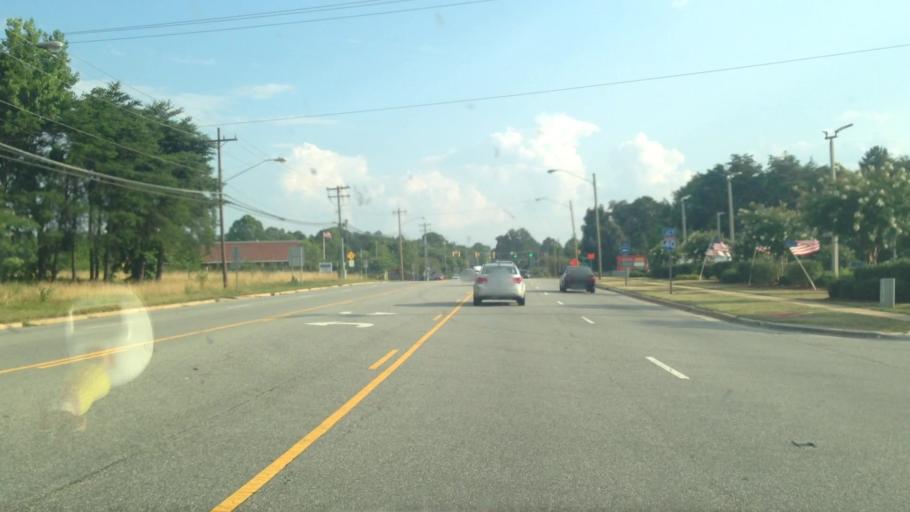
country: US
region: North Carolina
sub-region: Forsyth County
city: Kernersville
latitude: 36.0887
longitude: -80.0628
